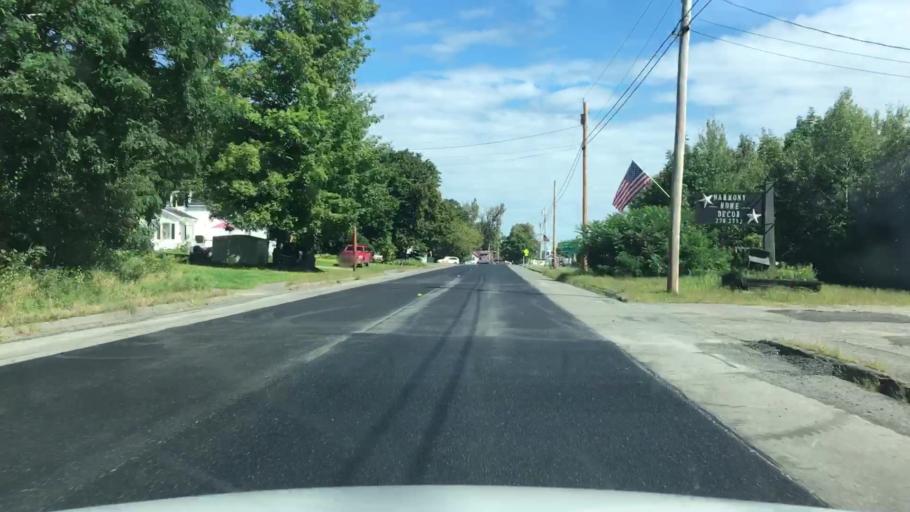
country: US
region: Maine
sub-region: Penobscot County
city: Corinna
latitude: 44.9150
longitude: -69.2634
